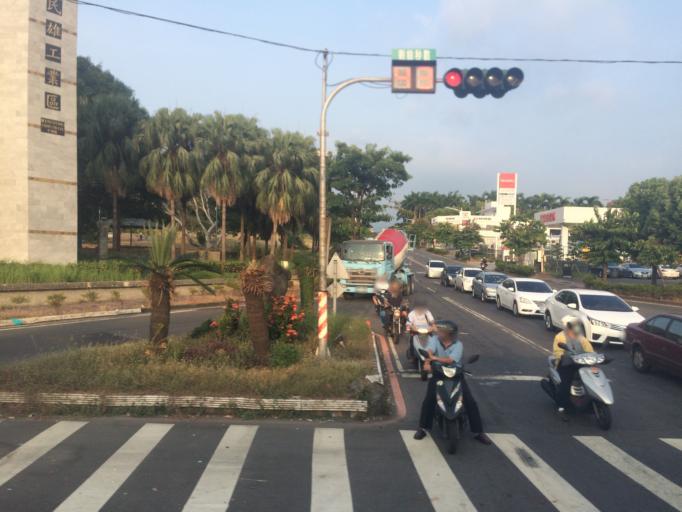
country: TW
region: Taiwan
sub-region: Chiayi
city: Jiayi Shi
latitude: 23.5202
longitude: 120.4405
